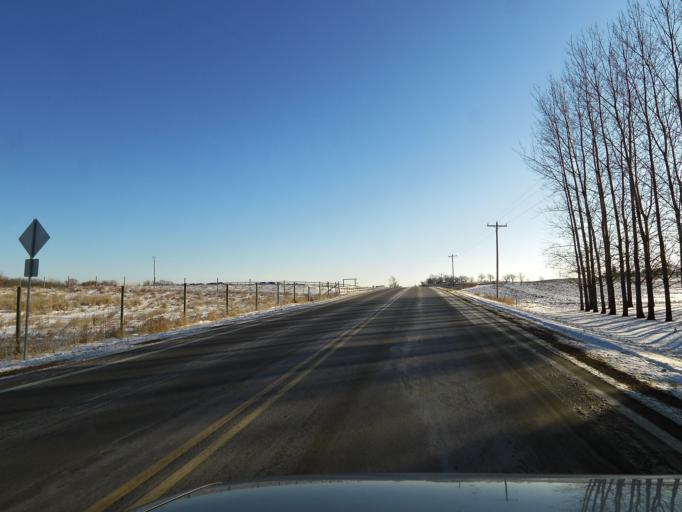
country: US
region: Minnesota
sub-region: Carver County
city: Carver
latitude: 44.7328
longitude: -93.5721
